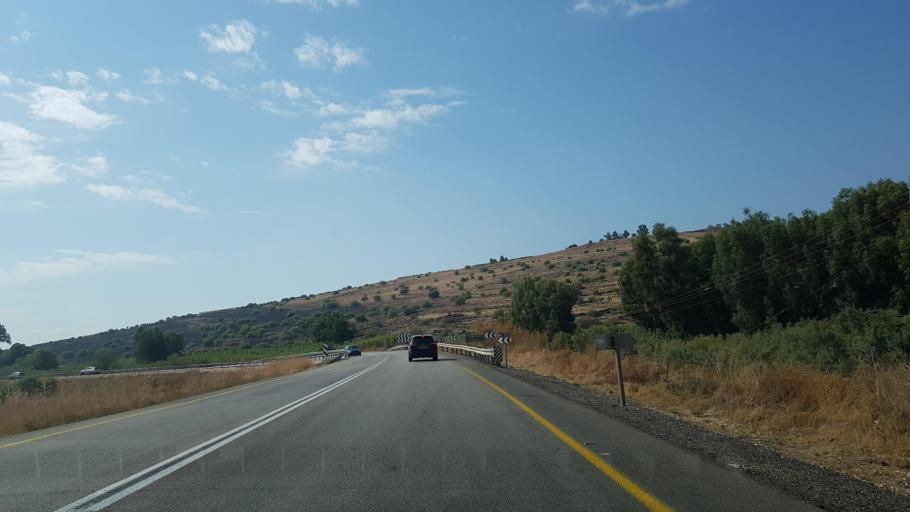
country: SY
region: Quneitra
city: Al Butayhah
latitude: 32.9044
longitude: 35.6194
